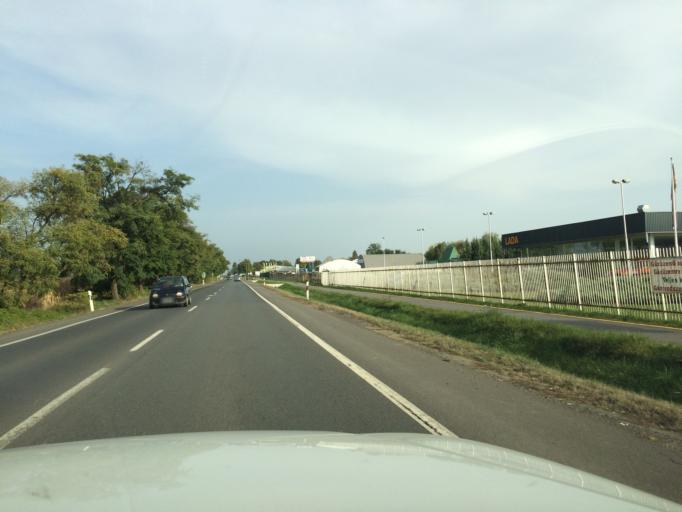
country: HU
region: Szabolcs-Szatmar-Bereg
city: Nyiregyhaza
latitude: 47.9567
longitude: 21.6663
